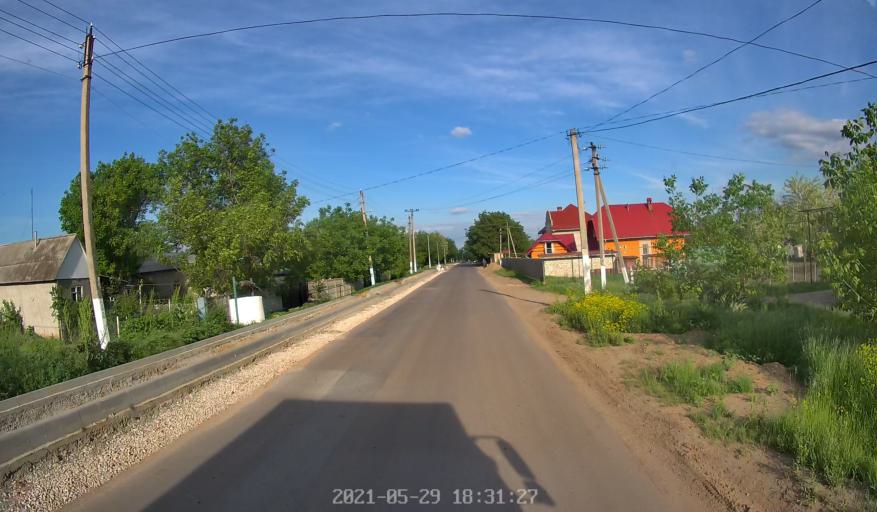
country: MD
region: Chisinau
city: Singera
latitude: 46.8196
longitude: 28.8848
